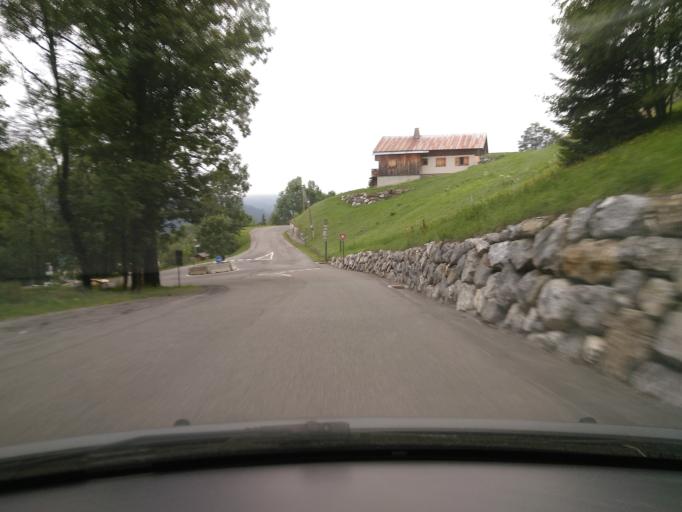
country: FR
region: Rhone-Alpes
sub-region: Departement de la Haute-Savoie
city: Le Grand-Bornand
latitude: 45.9130
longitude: 6.4620
